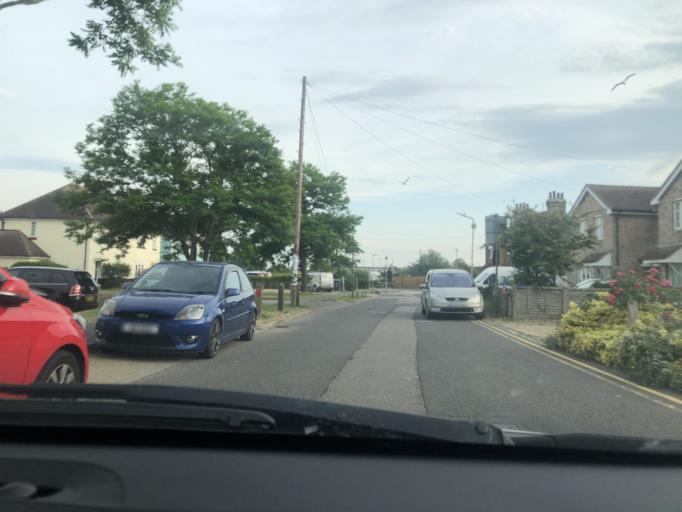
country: GB
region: England
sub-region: Kent
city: Herne Bay
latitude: 51.3672
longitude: 1.1741
